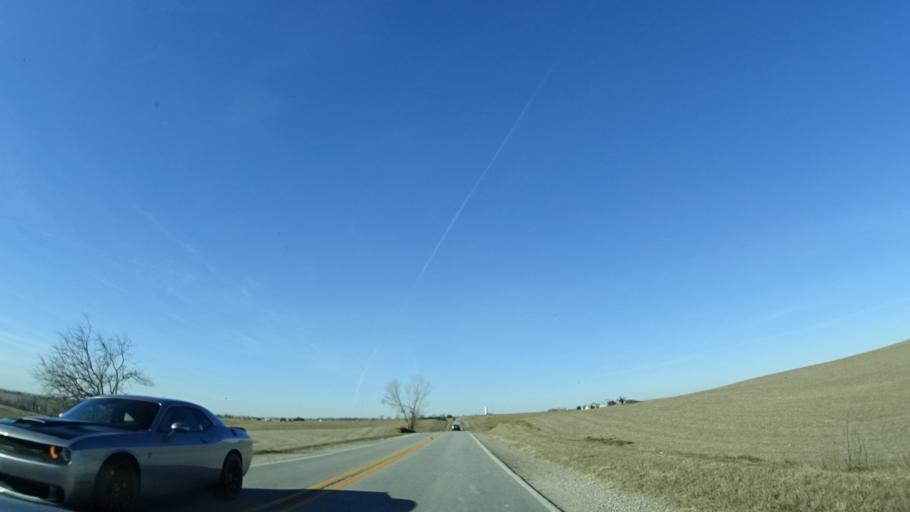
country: US
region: Nebraska
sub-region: Sarpy County
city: Springfield
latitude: 41.0889
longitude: -96.0881
